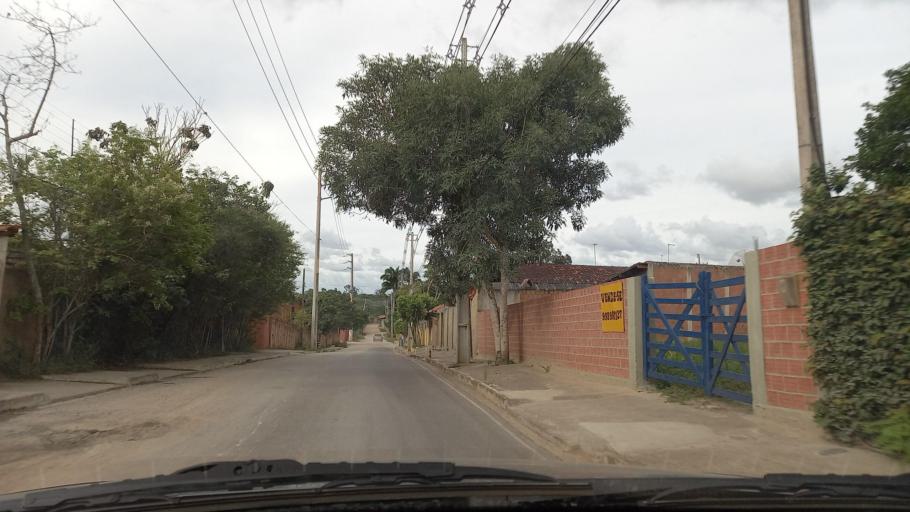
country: BR
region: Pernambuco
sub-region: Gravata
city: Gravata
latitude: -8.1986
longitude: -35.5419
